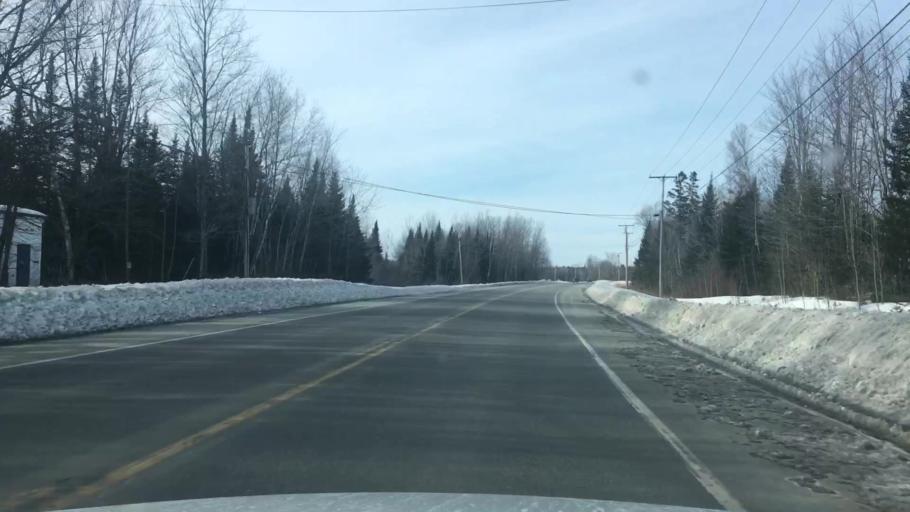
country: US
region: Maine
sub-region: Penobscot County
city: Kenduskeag
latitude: 44.9073
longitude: -68.8938
